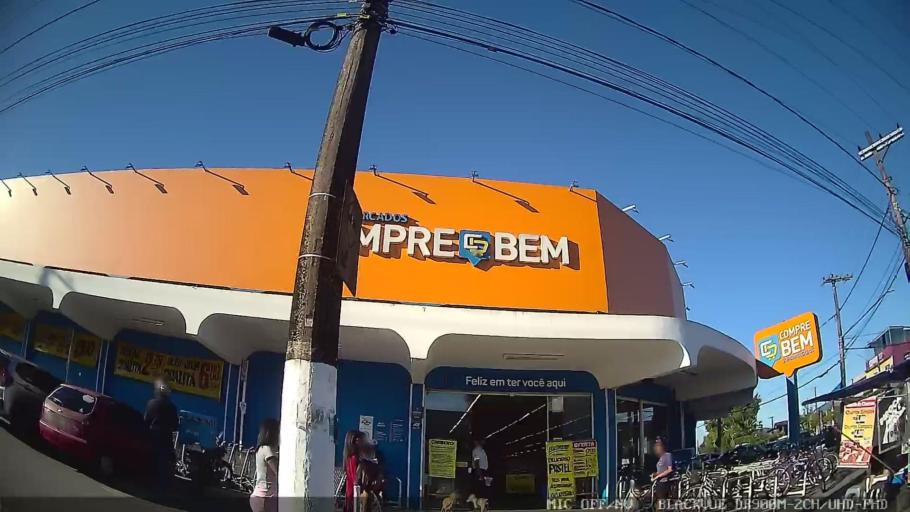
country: BR
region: Sao Paulo
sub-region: Santos
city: Santos
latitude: -23.9456
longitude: -46.2985
